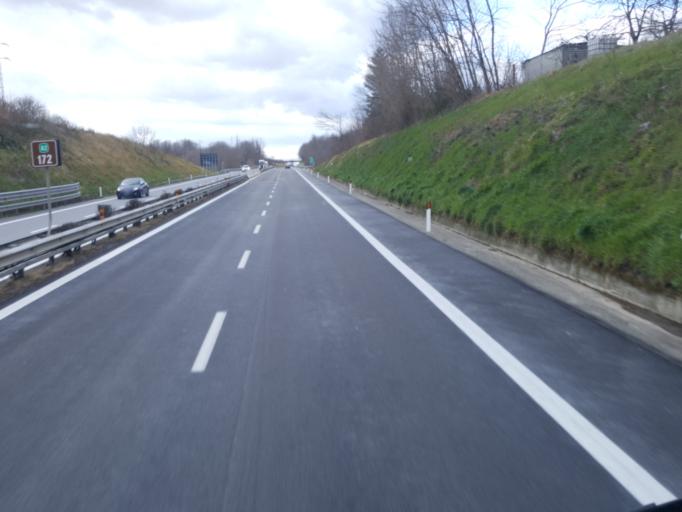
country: IT
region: Calabria
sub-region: Provincia di Cosenza
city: Santo Stefano di Rogliano
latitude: 39.2108
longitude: 16.3077
